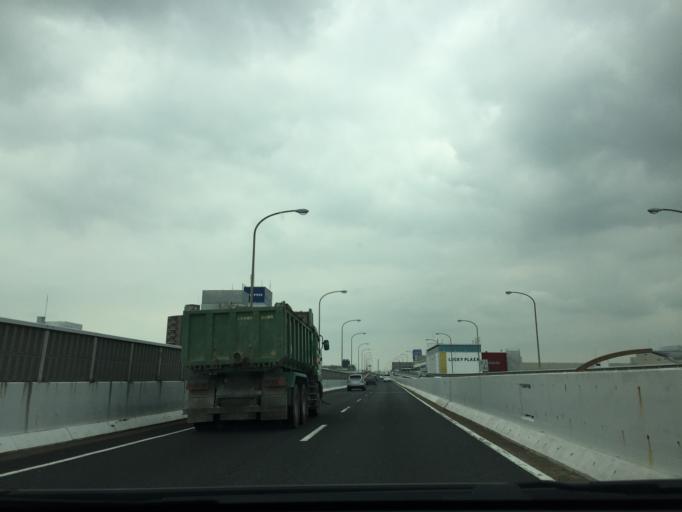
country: JP
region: Aichi
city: Nagoya-shi
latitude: 35.1120
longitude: 136.9224
